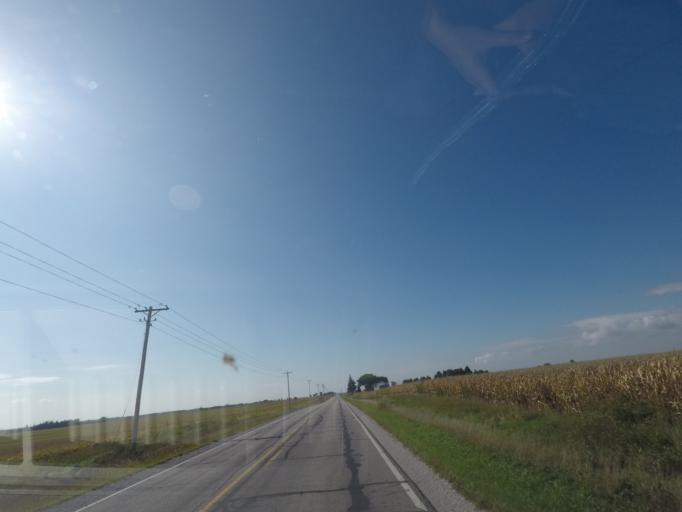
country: US
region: Iowa
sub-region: Story County
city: Nevada
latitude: 42.0437
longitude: -93.4058
